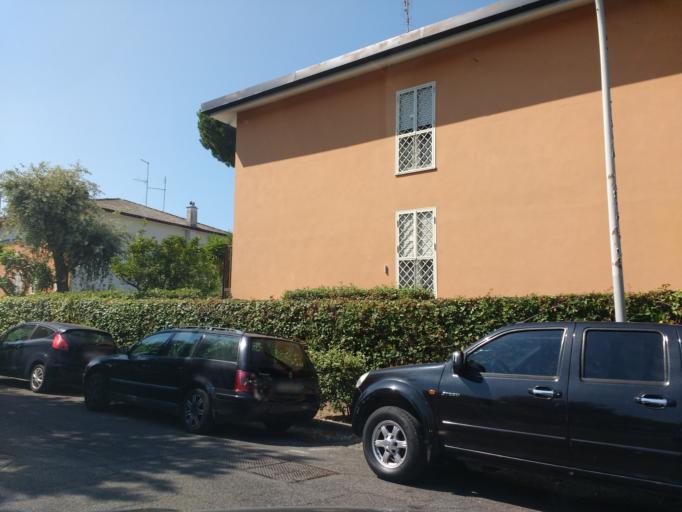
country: IT
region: Latium
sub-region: Citta metropolitana di Roma Capitale
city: Acilia-Castel Fusano-Ostia Antica
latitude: 41.7556
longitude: 12.3560
